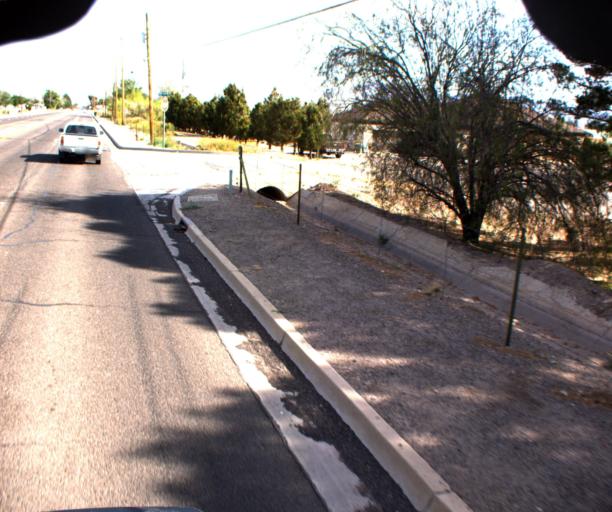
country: US
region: Arizona
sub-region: Graham County
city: Safford
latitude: 32.8073
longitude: -109.7076
